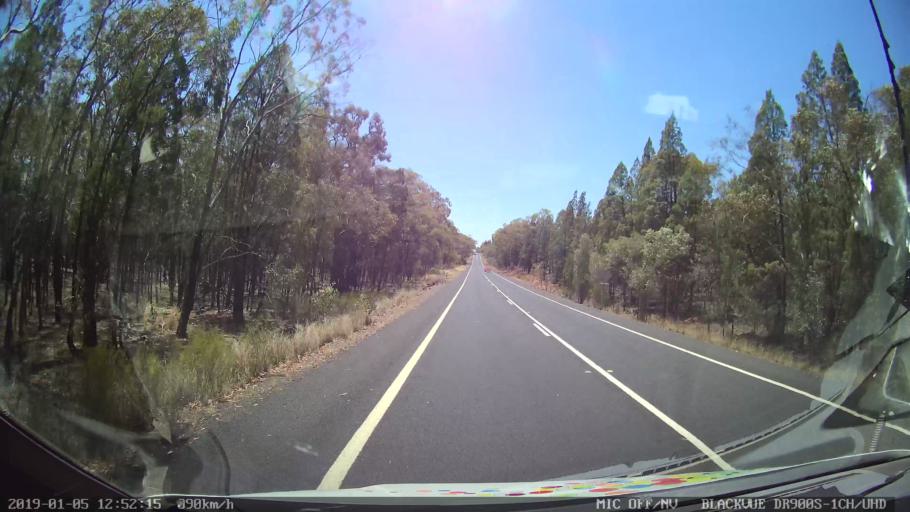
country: AU
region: New South Wales
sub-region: Warrumbungle Shire
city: Coonabarabran
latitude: -31.1216
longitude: 149.6531
